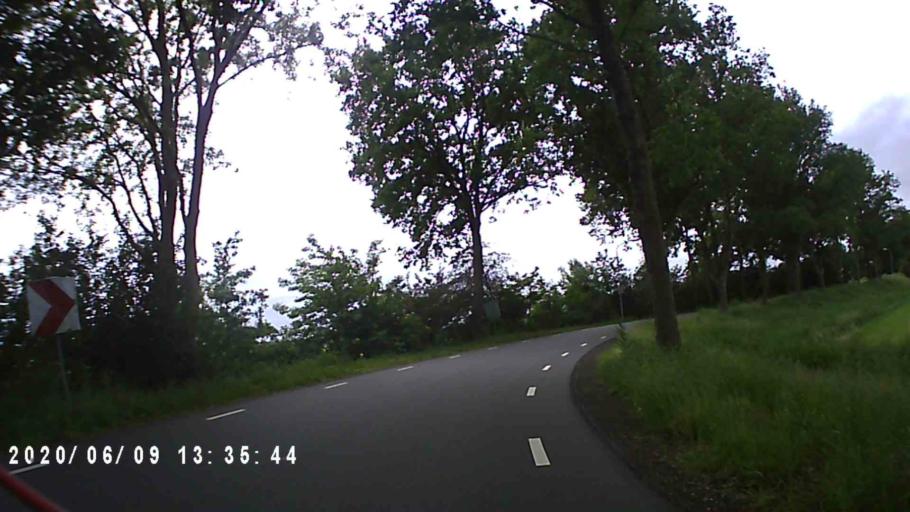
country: NL
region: Groningen
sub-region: Gemeente Haren
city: Haren
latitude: 53.2088
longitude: 6.6608
